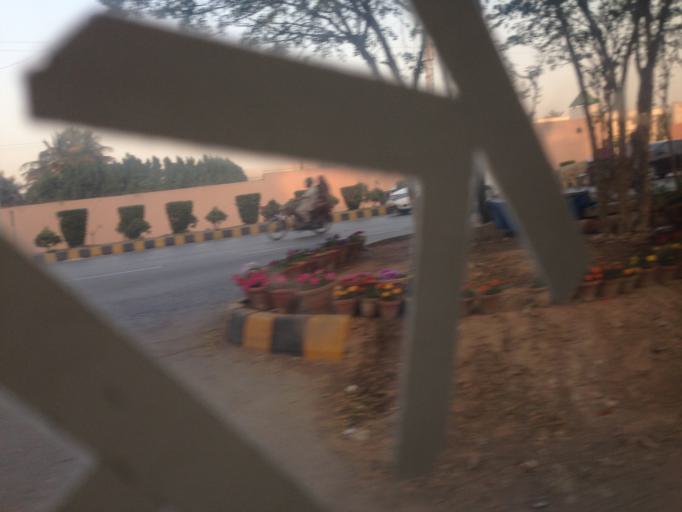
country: PK
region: Sindh
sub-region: Karachi District
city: Karachi
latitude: 24.8825
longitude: 67.0908
